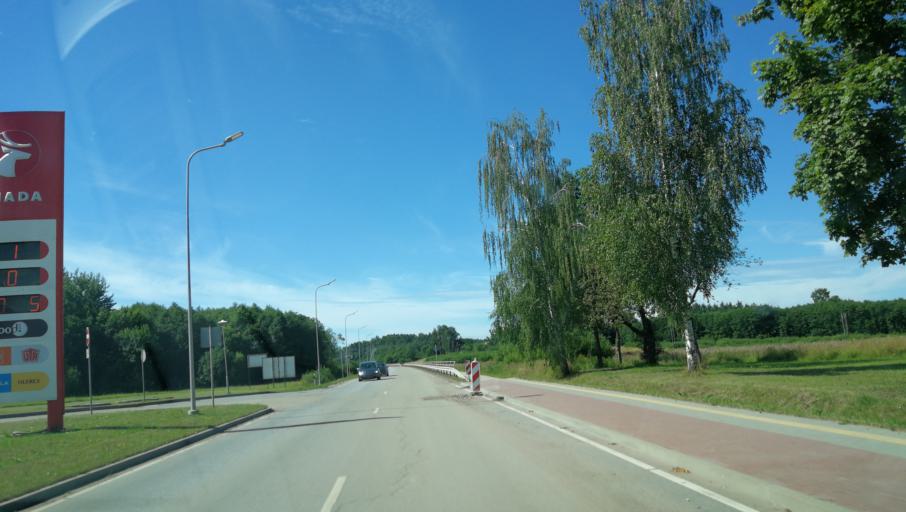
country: LV
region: Gulbenes Rajons
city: Gulbene
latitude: 57.1720
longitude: 26.7406
